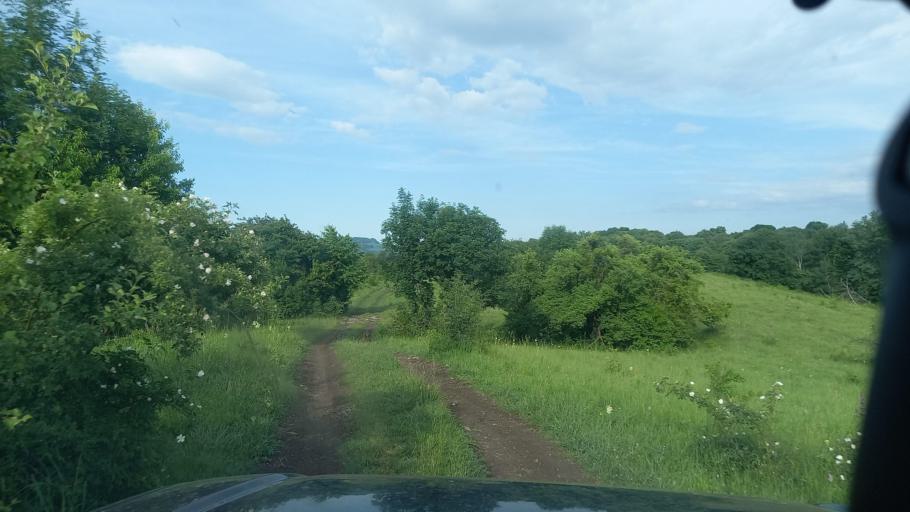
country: RU
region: Karachayevo-Cherkesiya
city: Kurdzhinovo
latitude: 44.1262
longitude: 41.0751
